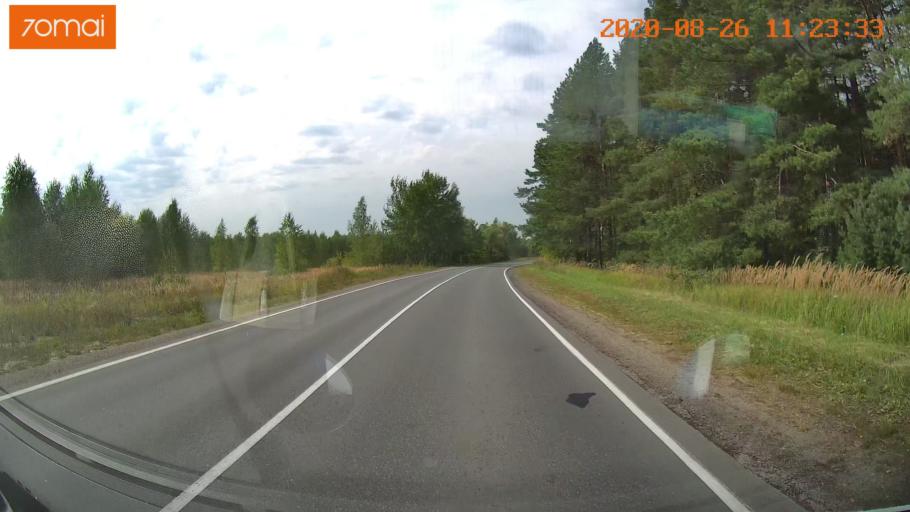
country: RU
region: Rjazan
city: Shilovo
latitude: 54.3510
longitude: 41.0084
